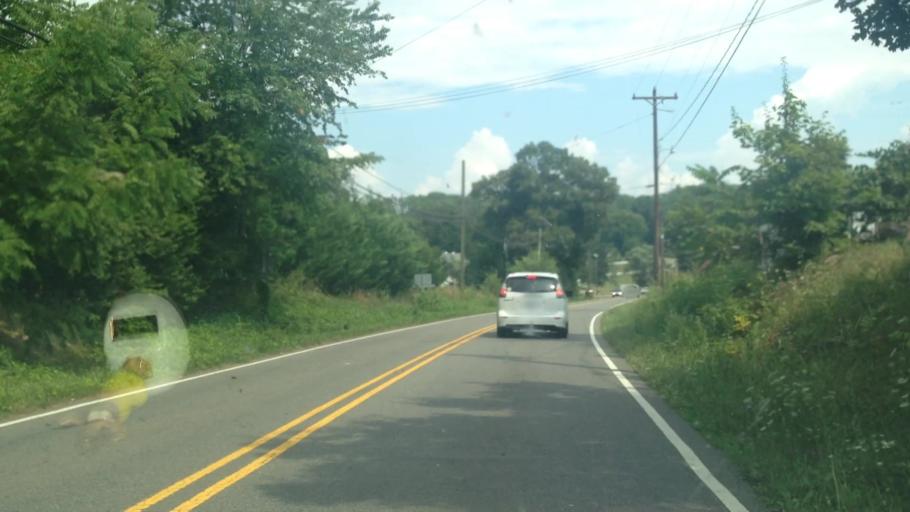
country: US
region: North Carolina
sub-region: Surry County
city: Mount Airy
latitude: 36.4850
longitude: -80.5880
